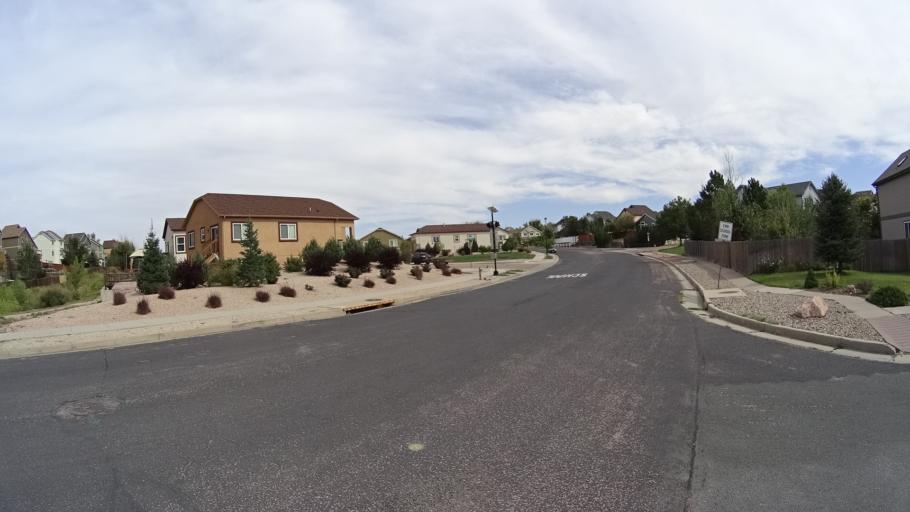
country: US
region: Colorado
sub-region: El Paso County
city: Cimarron Hills
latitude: 38.9051
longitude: -104.6993
